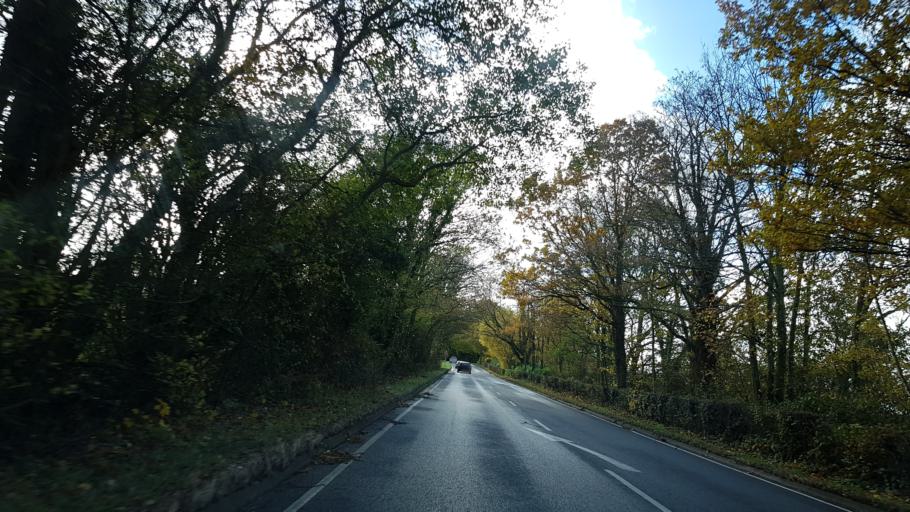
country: GB
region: England
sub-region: Surrey
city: Haslemere
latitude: 51.1260
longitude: -0.6731
